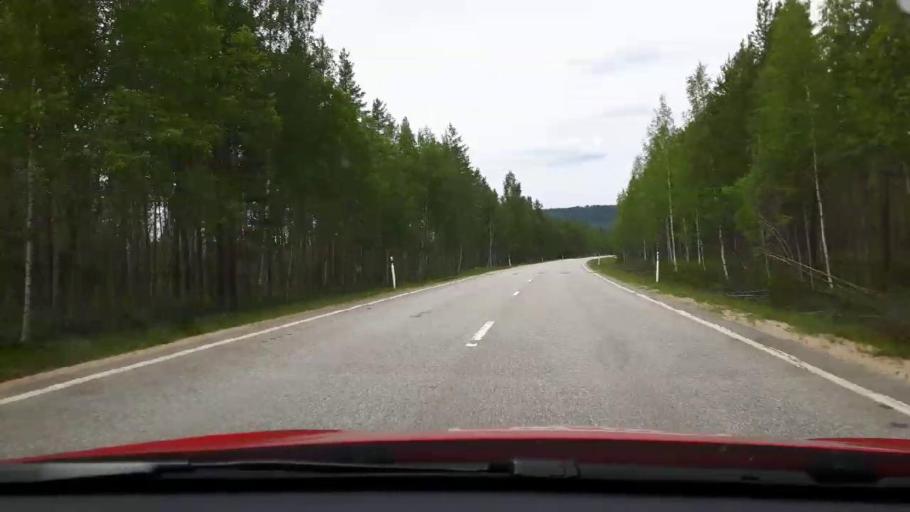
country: SE
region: Jaemtland
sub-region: Harjedalens Kommun
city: Sveg
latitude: 62.0819
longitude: 14.2563
